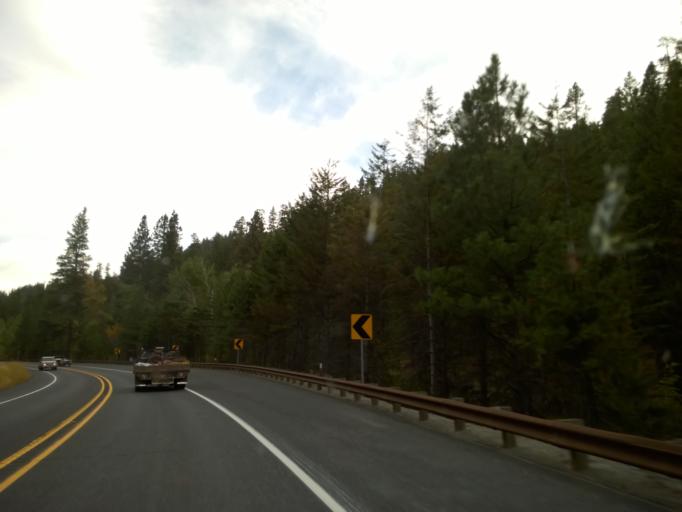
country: US
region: Washington
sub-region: Chelan County
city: Leavenworth
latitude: 47.4134
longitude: -120.6587
